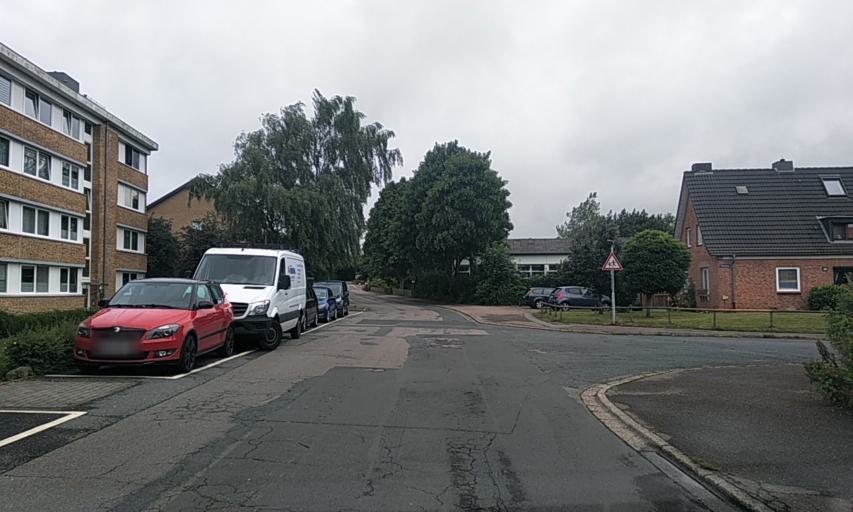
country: DE
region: Schleswig-Holstein
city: Schleswig
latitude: 54.5247
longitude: 9.5451
